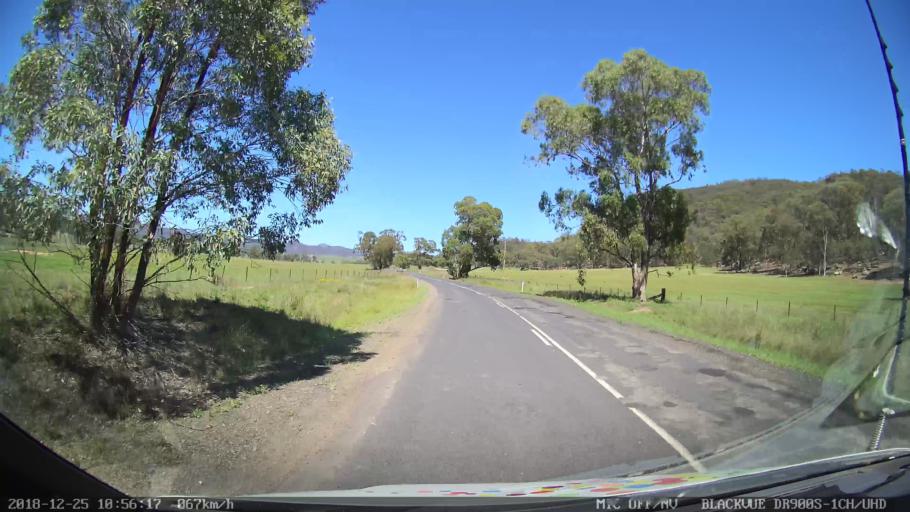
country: AU
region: New South Wales
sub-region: Upper Hunter Shire
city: Merriwa
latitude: -32.4005
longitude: 150.2643
